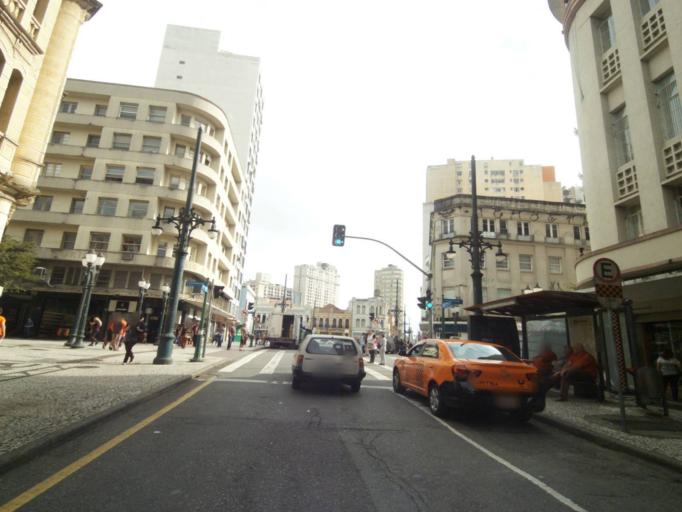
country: BR
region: Parana
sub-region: Curitiba
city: Curitiba
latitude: -25.4304
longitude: -49.2691
